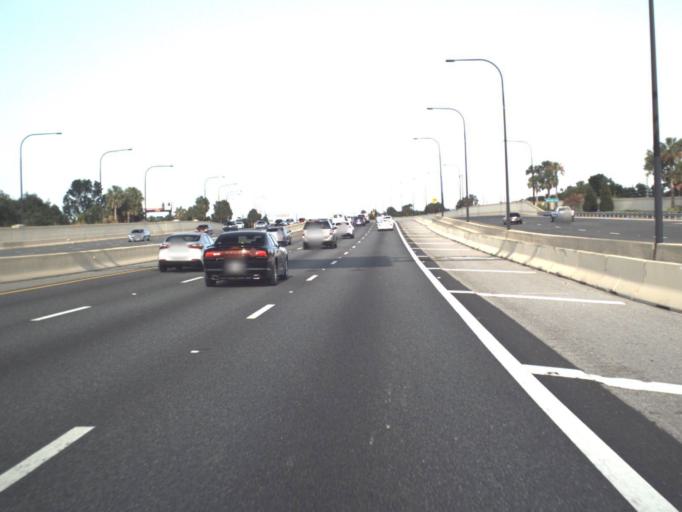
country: US
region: Florida
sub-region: Orange County
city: Azalea Park
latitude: 28.5396
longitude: -81.3164
